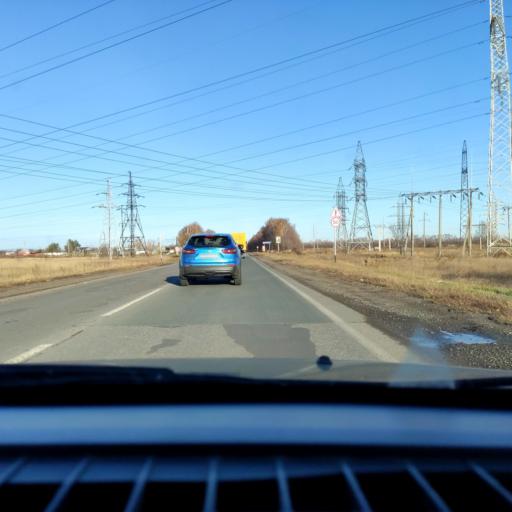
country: RU
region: Samara
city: Tol'yatti
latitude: 53.5864
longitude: 49.3320
